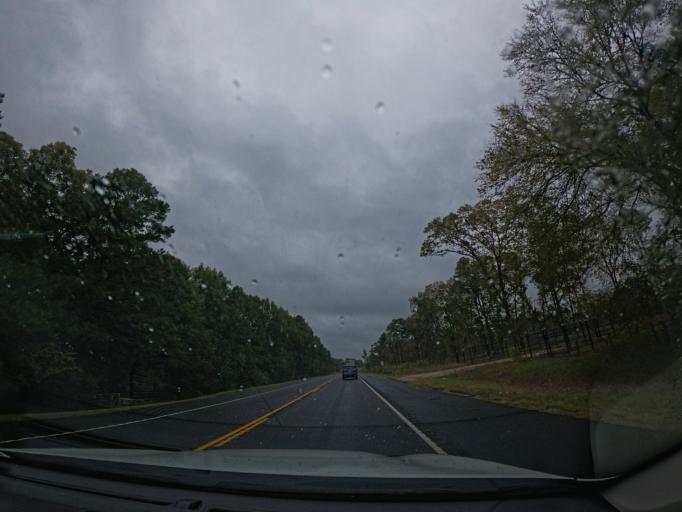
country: US
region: Louisiana
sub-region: Caddo Parish
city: Greenwood
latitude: 32.4311
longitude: -93.9844
